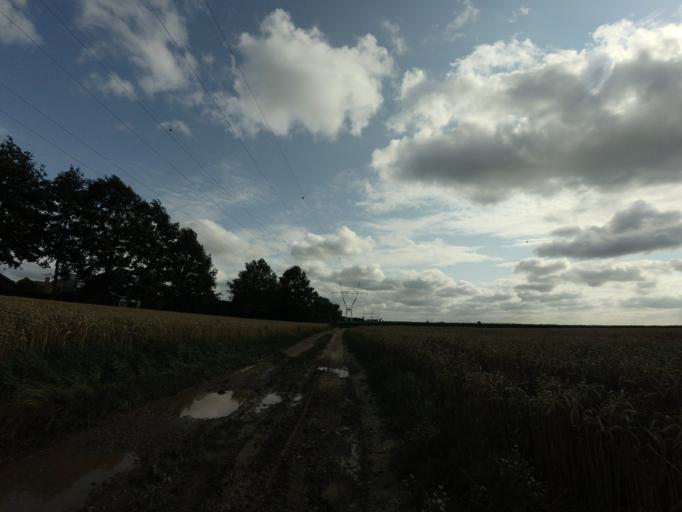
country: BE
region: Flanders
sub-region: Provincie Vlaams-Brabant
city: Vilvoorde
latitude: 50.9370
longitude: 4.4016
